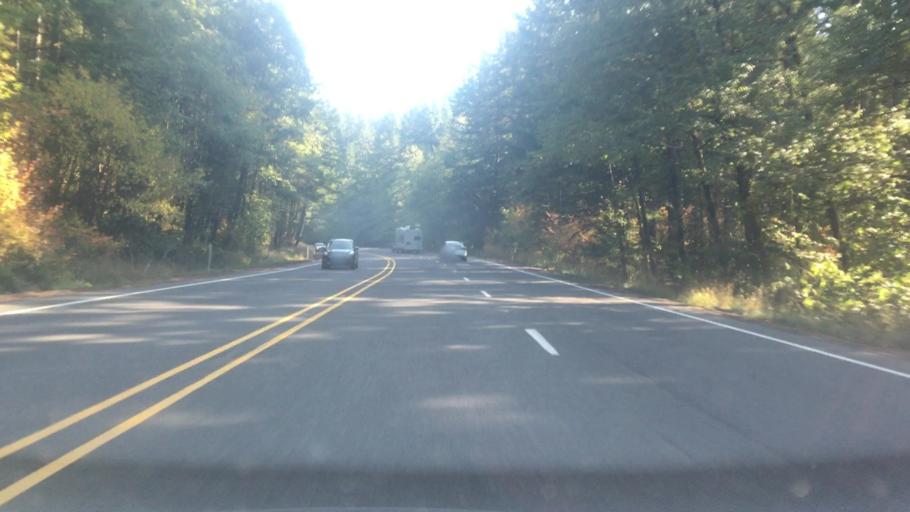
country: US
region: Oregon
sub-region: Polk County
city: Grand Ronde
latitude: 45.0620
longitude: -123.7024
